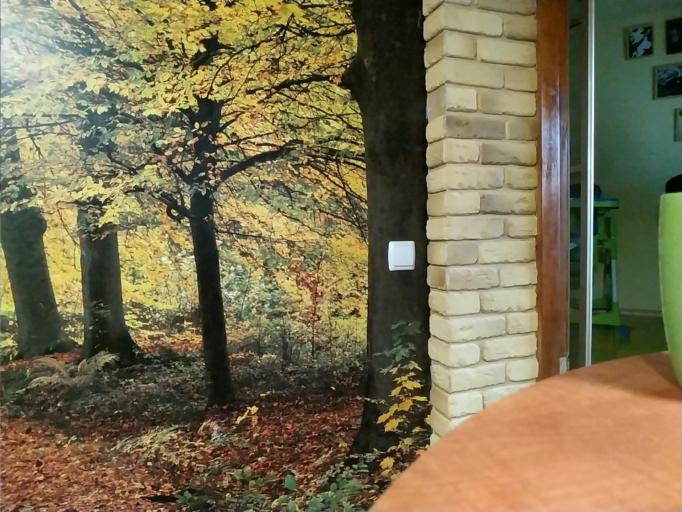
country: RU
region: Tverskaya
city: Staraya Toropa
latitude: 56.3505
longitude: 31.8156
